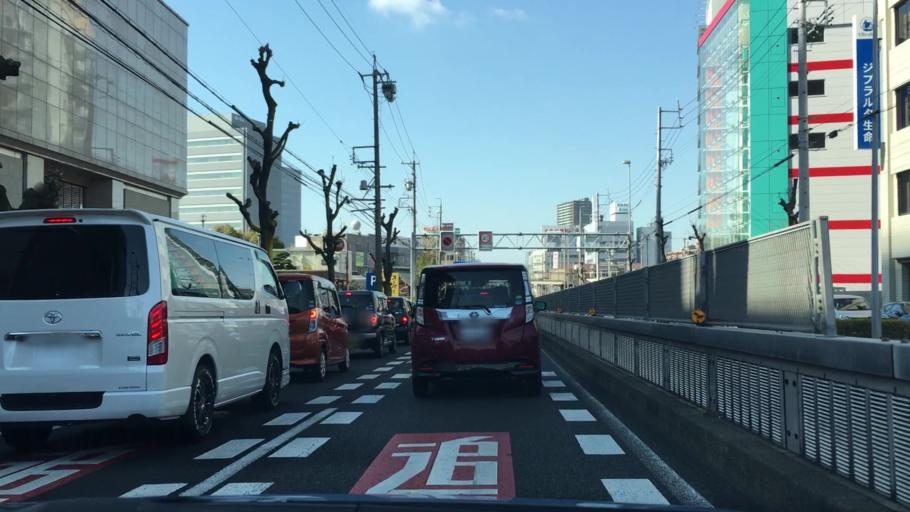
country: JP
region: Aichi
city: Okazaki
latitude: 34.9551
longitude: 137.1708
